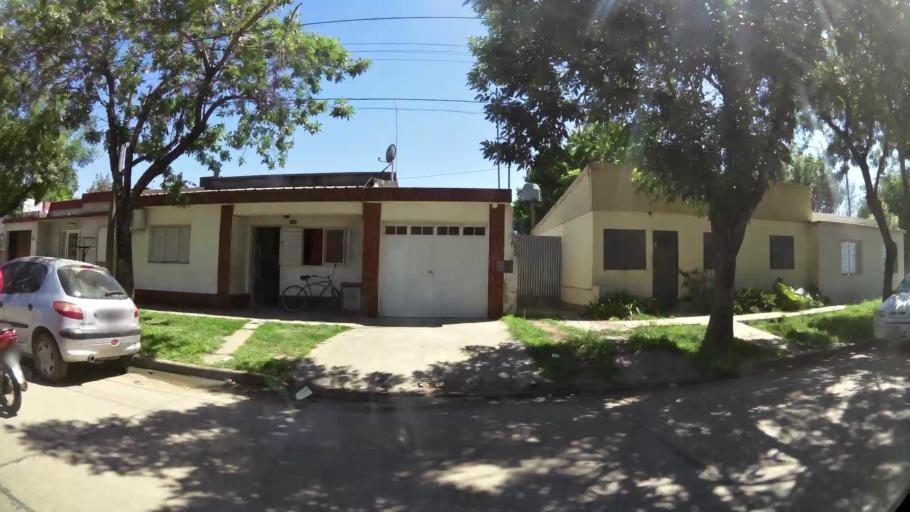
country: AR
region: Santa Fe
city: Esperanza
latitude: -31.4369
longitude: -60.9308
